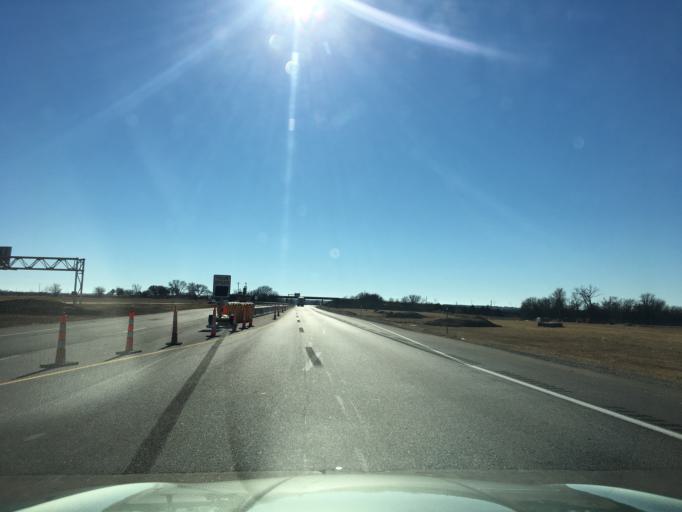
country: US
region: Kansas
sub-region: Sumner County
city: Wellington
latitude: 37.2366
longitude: -97.3392
